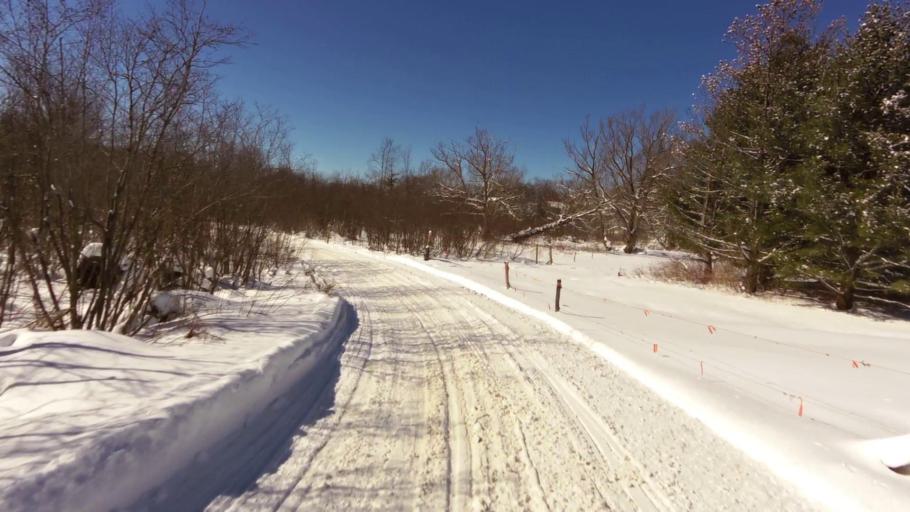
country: US
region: New York
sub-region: Chautauqua County
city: Mayville
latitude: 42.1578
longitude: -79.5887
